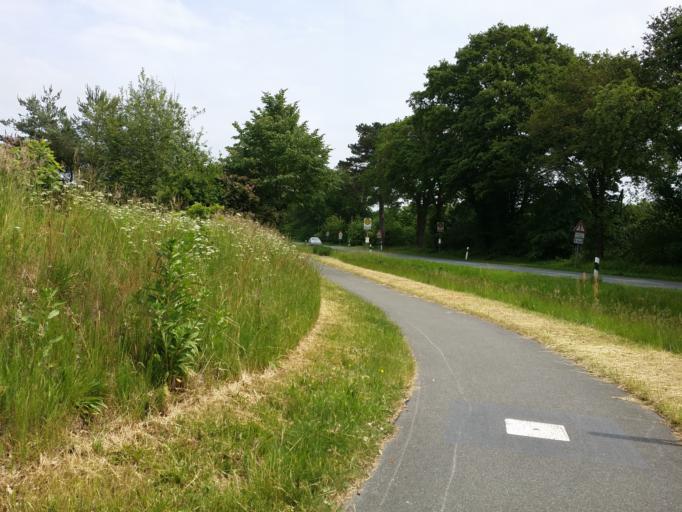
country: DE
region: Lower Saxony
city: Friedeburg
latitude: 53.4131
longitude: 7.8911
